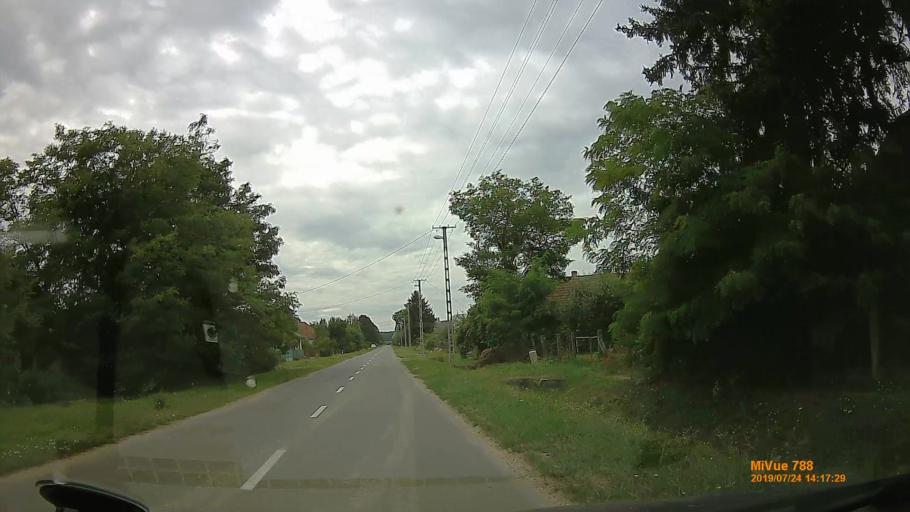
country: HU
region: Szabolcs-Szatmar-Bereg
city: Mandok
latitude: 48.3150
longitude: 22.2835
